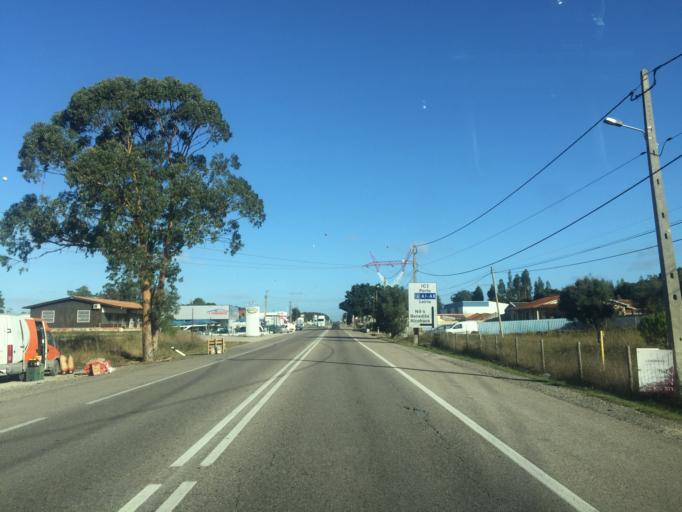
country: PT
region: Leiria
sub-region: Alcobaca
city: Benedita
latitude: 39.4020
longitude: -8.9609
